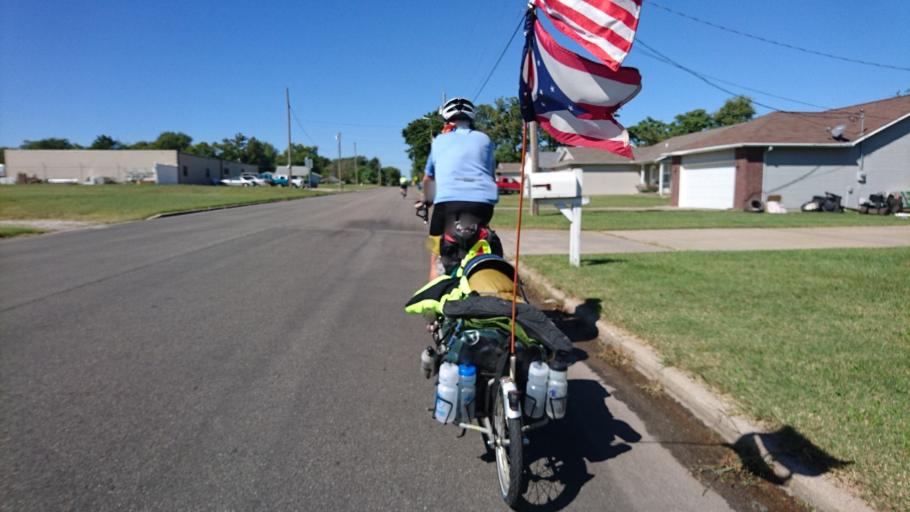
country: US
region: Missouri
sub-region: Jasper County
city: Joplin
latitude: 37.0904
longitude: -94.5380
